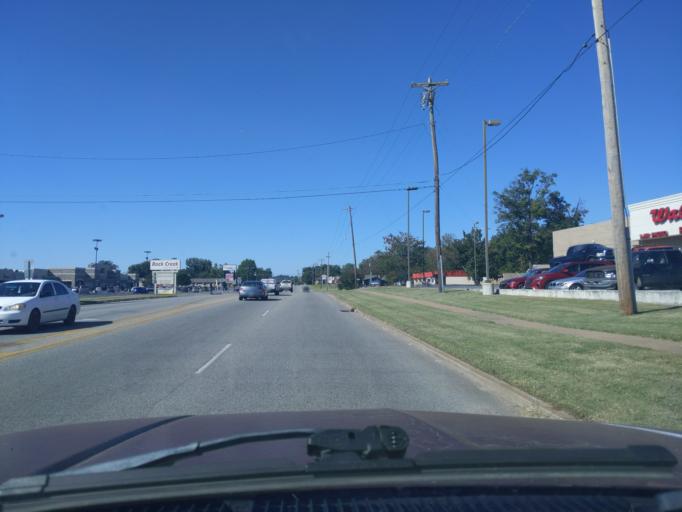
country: US
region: Oklahoma
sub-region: Creek County
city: Sapulpa
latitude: 35.9885
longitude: -96.1140
